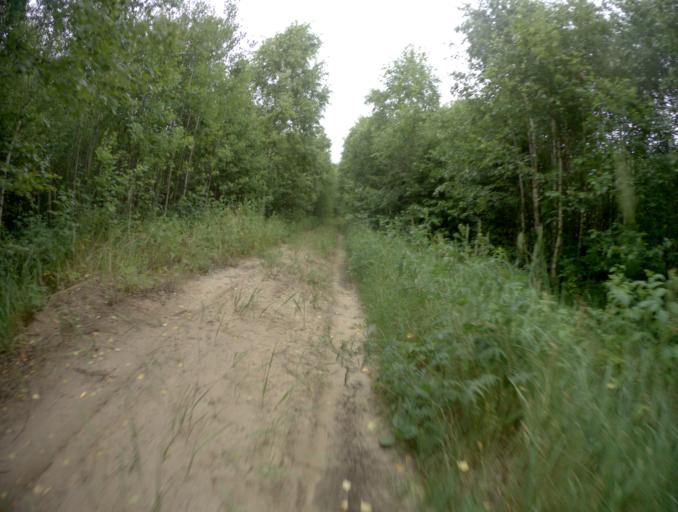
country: RU
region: Nizjnij Novgorod
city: Frolishchi
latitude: 56.5345
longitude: 42.6184
